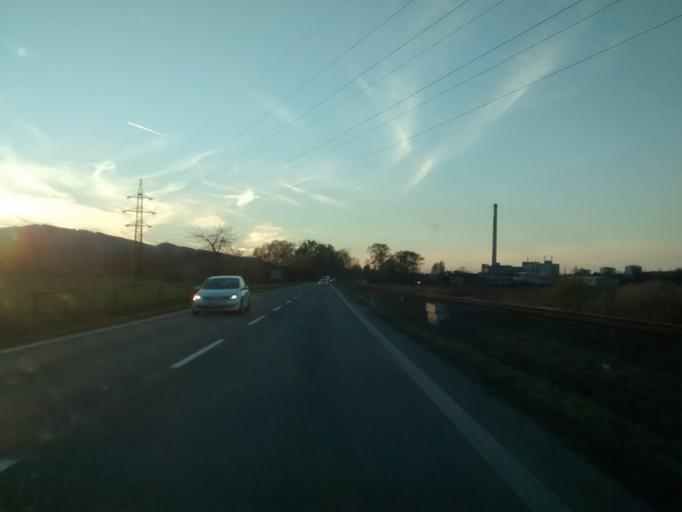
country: CZ
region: Zlin
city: Zubri
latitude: 49.4602
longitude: 18.1018
